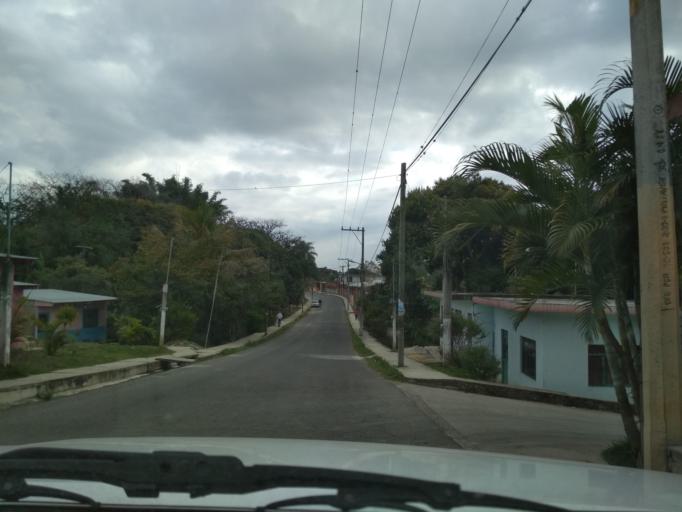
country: MX
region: Veracruz
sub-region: Coatepec
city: Tuzamapan
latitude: 19.3697
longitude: -96.8835
